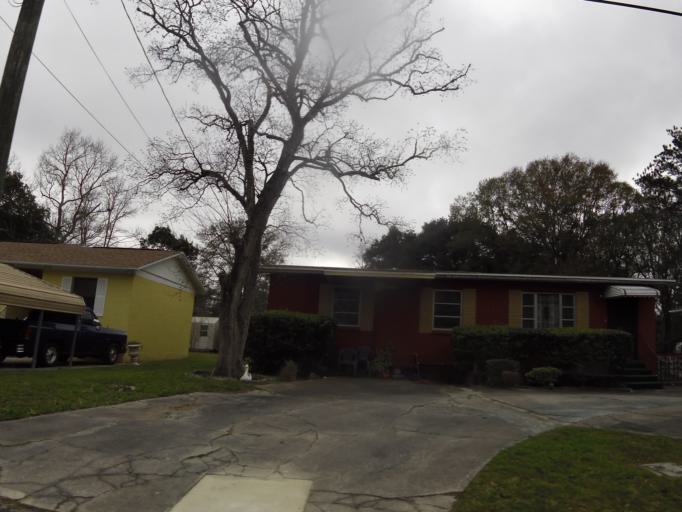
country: US
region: Florida
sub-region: Duval County
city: Jacksonville
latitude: 30.3700
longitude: -81.7161
